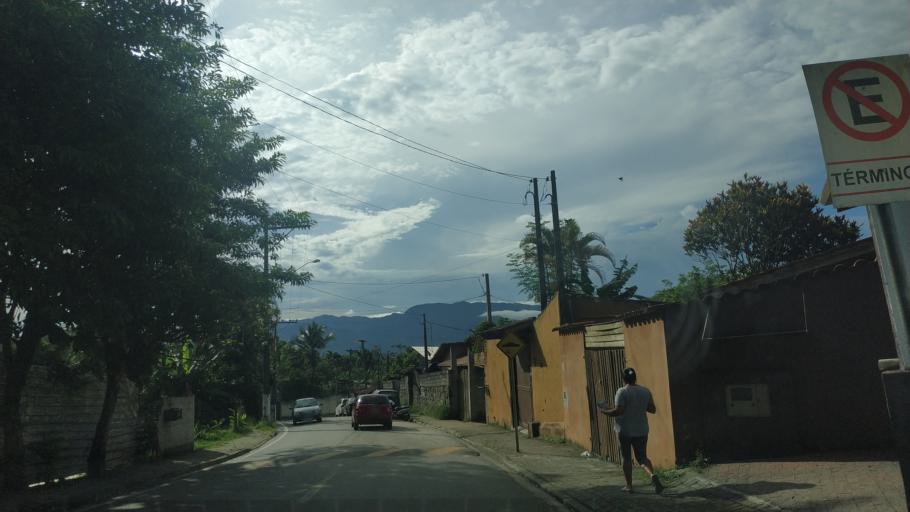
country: BR
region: Sao Paulo
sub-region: Ilhabela
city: Ilhabela
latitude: -23.8291
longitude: -45.3557
